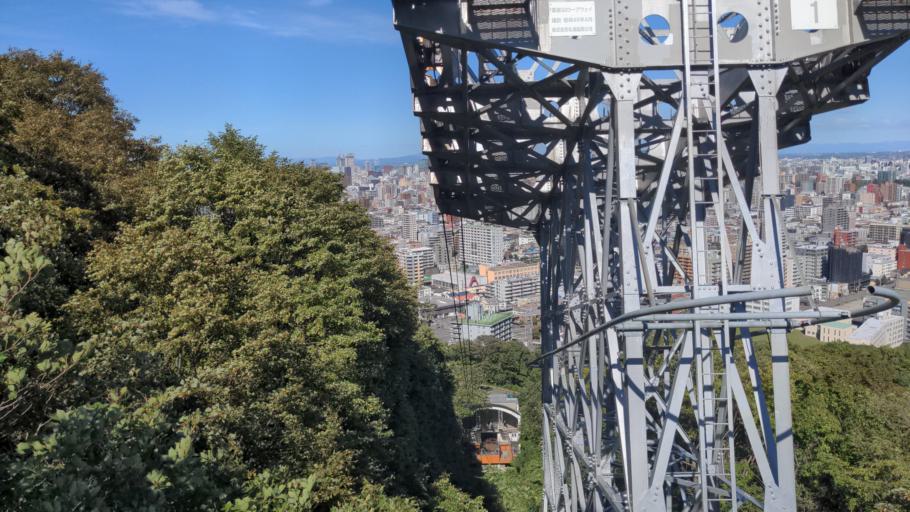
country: JP
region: Hokkaido
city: Sapporo
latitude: 43.0303
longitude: 141.3320
